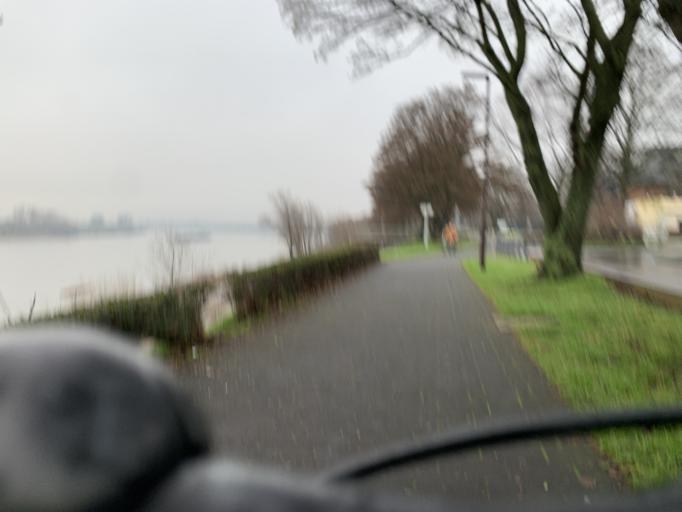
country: DE
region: North Rhine-Westphalia
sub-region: Regierungsbezirk Dusseldorf
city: Hochfeld
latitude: 51.3891
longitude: 6.7413
